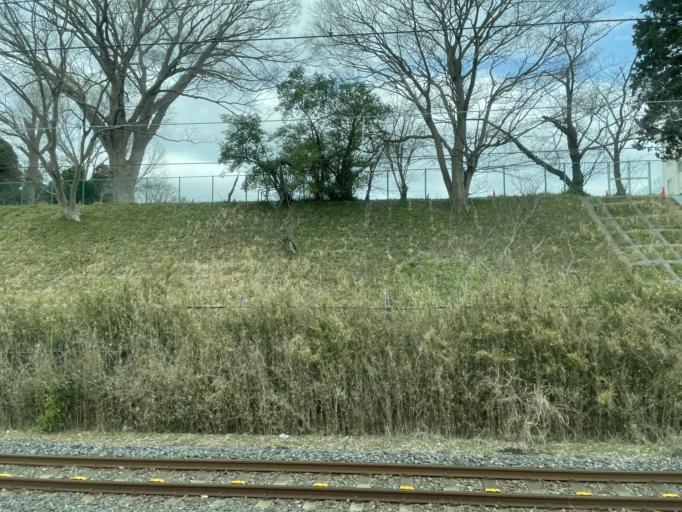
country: JP
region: Chiba
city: Narita
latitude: 35.7829
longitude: 140.3130
